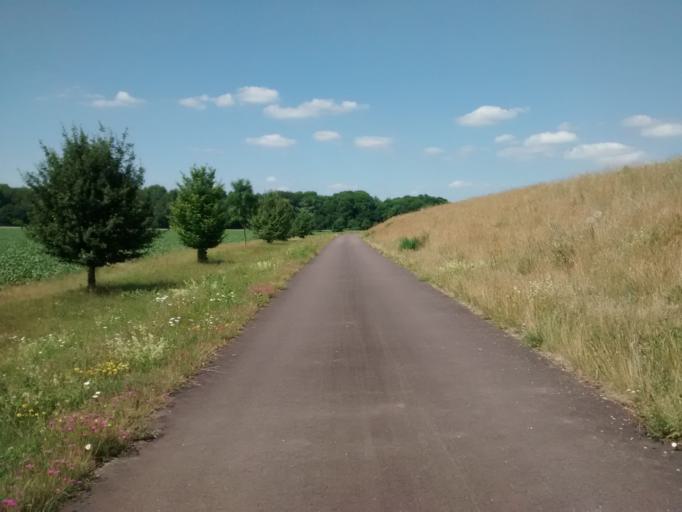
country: DE
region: Saxony-Anhalt
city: Coswig
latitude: 51.8396
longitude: 12.4944
